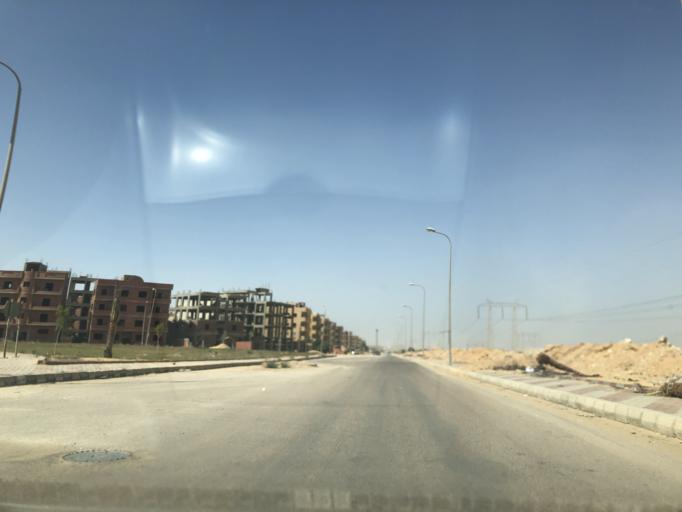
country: EG
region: Al Jizah
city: Madinat Sittah Uktubar
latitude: 29.9163
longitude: 31.0508
